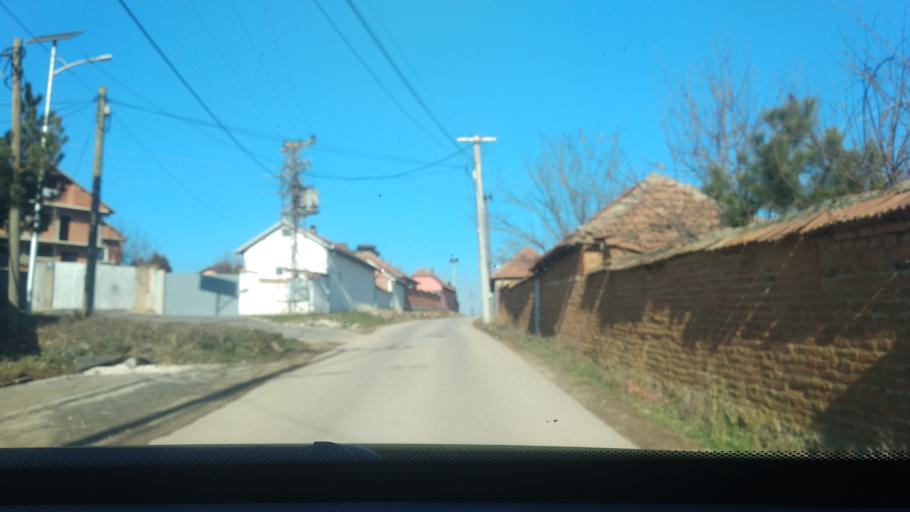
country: XK
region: Pristina
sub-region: Komuna e Gracanices
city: Glanica
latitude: 42.6058
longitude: 21.0283
